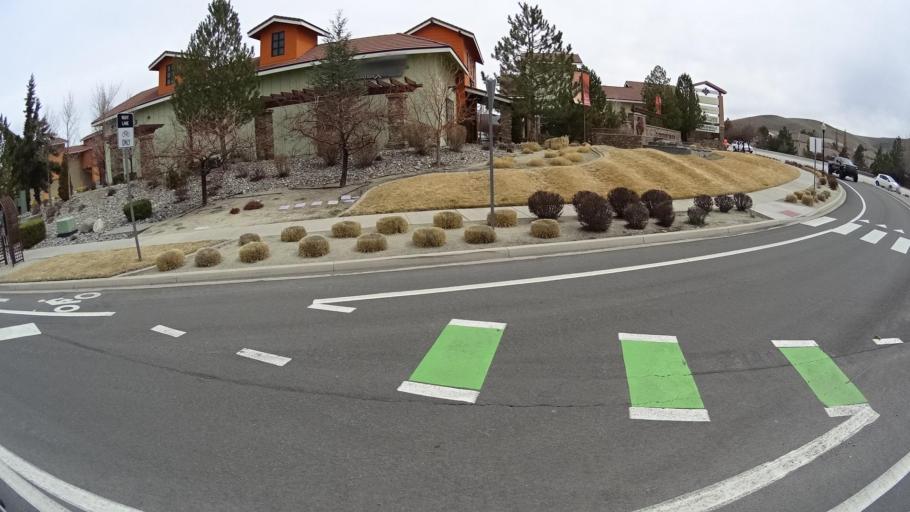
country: US
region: Nevada
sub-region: Washoe County
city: Spanish Springs
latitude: 39.6074
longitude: -119.6963
